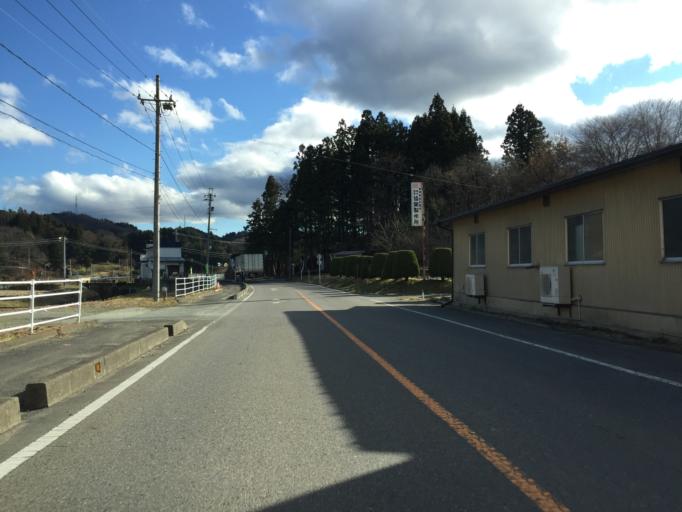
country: JP
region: Fukushima
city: Funehikimachi-funehiki
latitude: 37.5861
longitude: 140.5769
